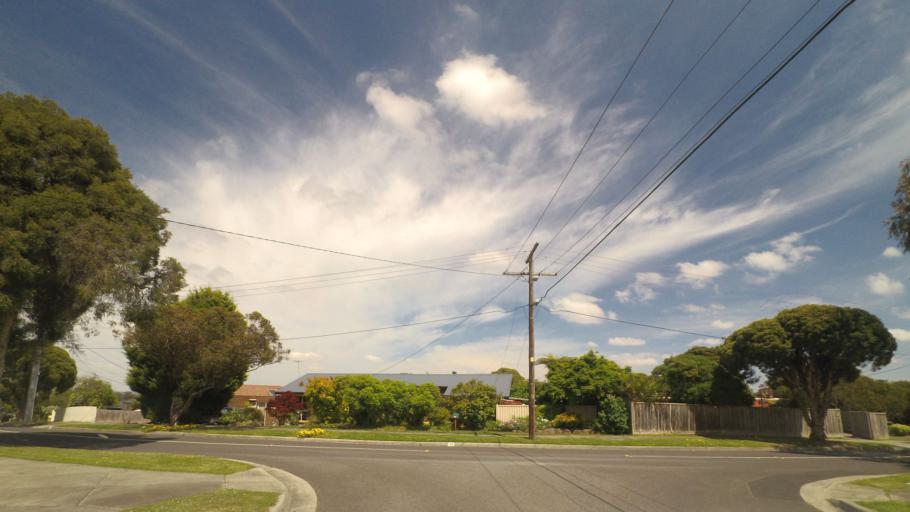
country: AU
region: Victoria
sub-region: Knox
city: Bayswater
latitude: -37.8497
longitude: 145.2511
